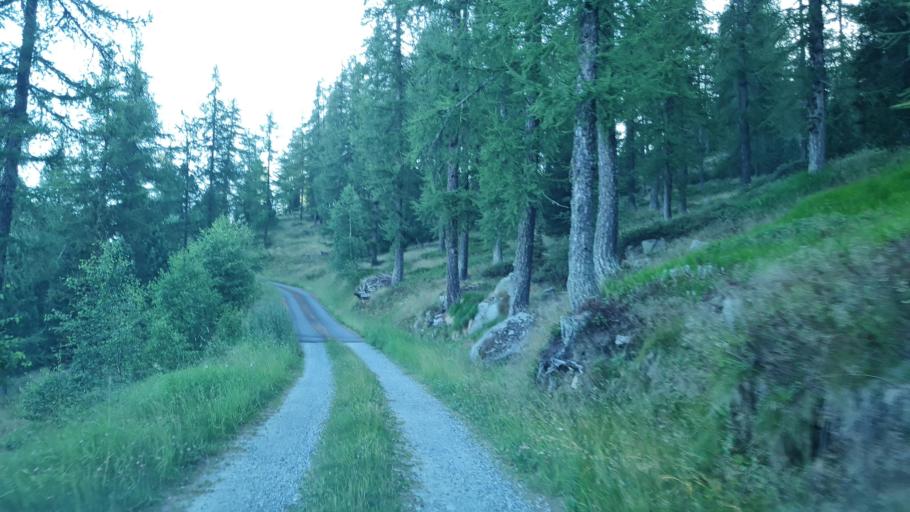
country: IT
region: Aosta Valley
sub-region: Valle d'Aosta
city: Fontainemore
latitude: 45.6252
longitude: 7.8731
